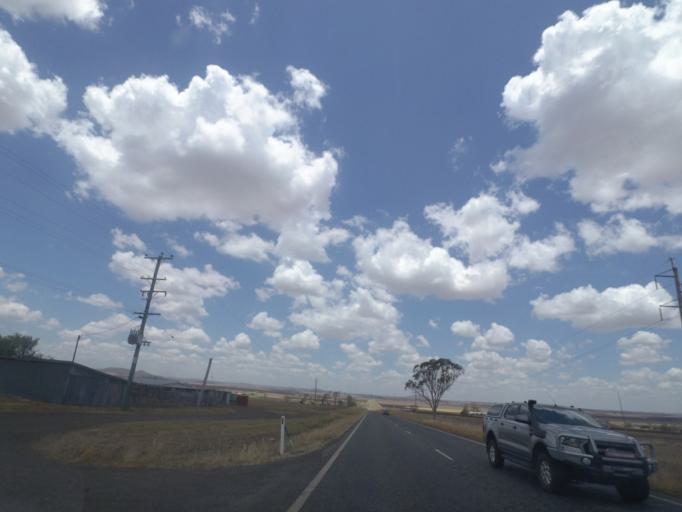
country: AU
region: Queensland
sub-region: Toowoomba
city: Top Camp
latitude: -27.8882
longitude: 151.9722
